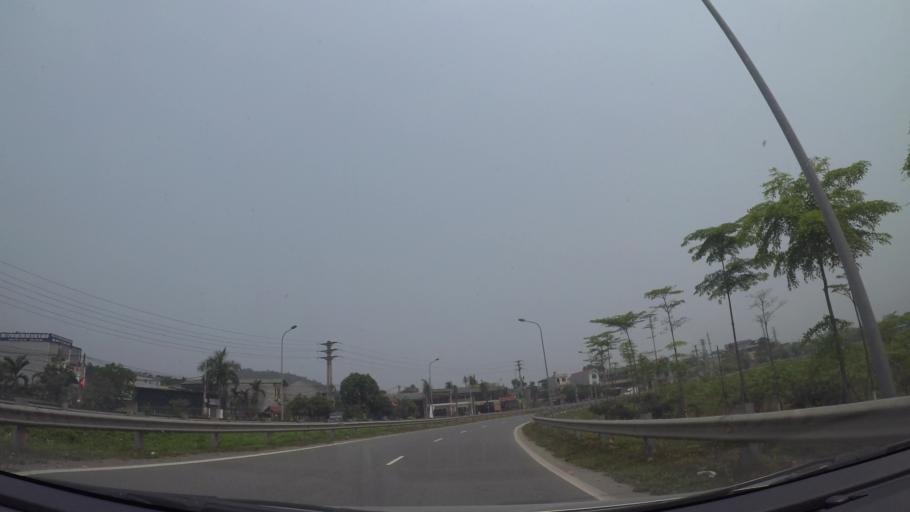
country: VN
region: Ha Noi
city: Lien Quan
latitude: 20.9917
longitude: 105.5219
